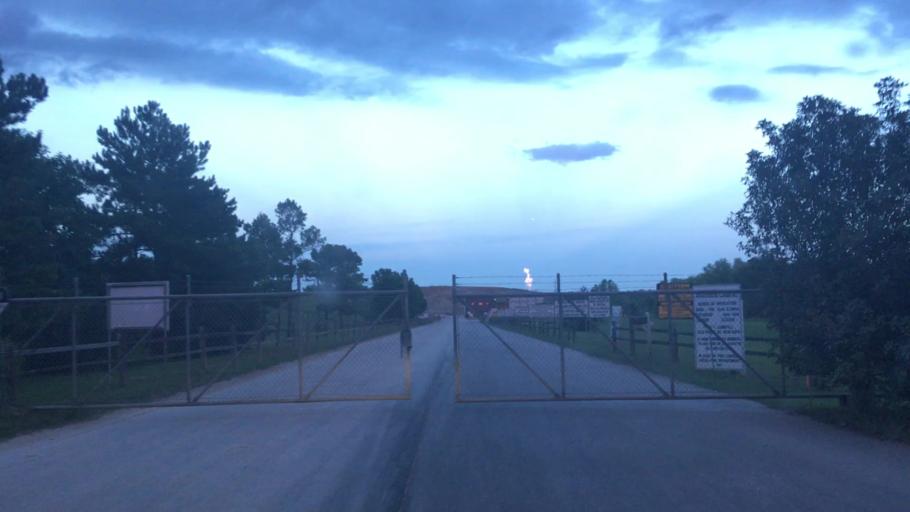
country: US
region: Texas
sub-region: Harris County
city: Humble
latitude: 29.9554
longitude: -95.2479
